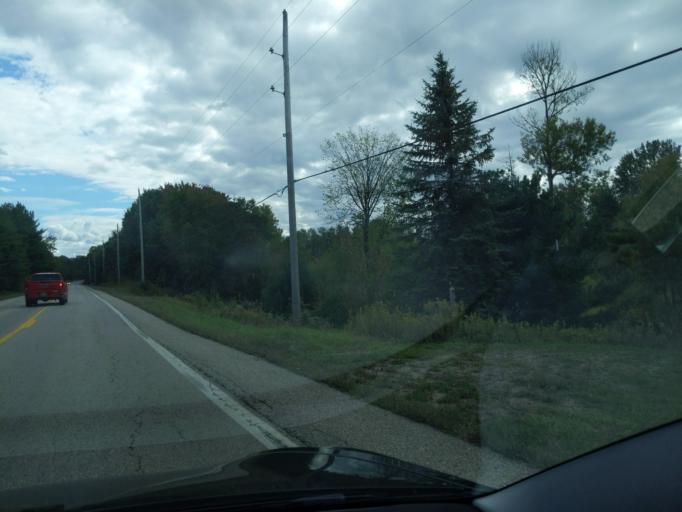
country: US
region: Michigan
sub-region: Kalkaska County
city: Rapid City
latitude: 44.9079
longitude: -85.2820
